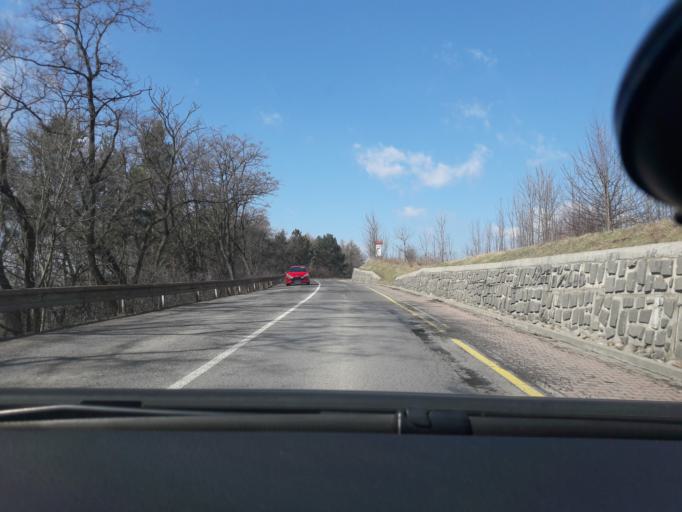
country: SK
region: Zilinsky
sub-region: Okres Liptovsky Mikulas
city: Liptovsky Mikulas
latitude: 49.0969
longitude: 19.5843
